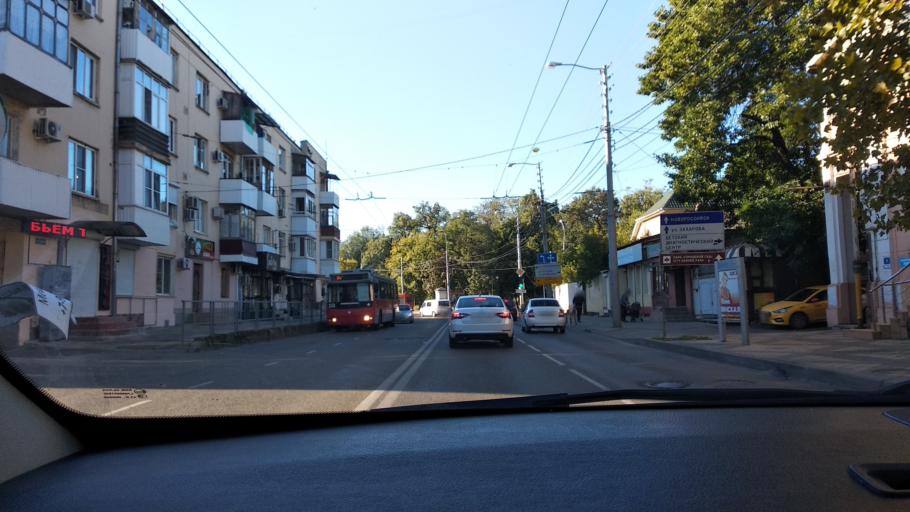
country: RU
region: Krasnodarskiy
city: Krasnodar
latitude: 45.0146
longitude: 38.9739
